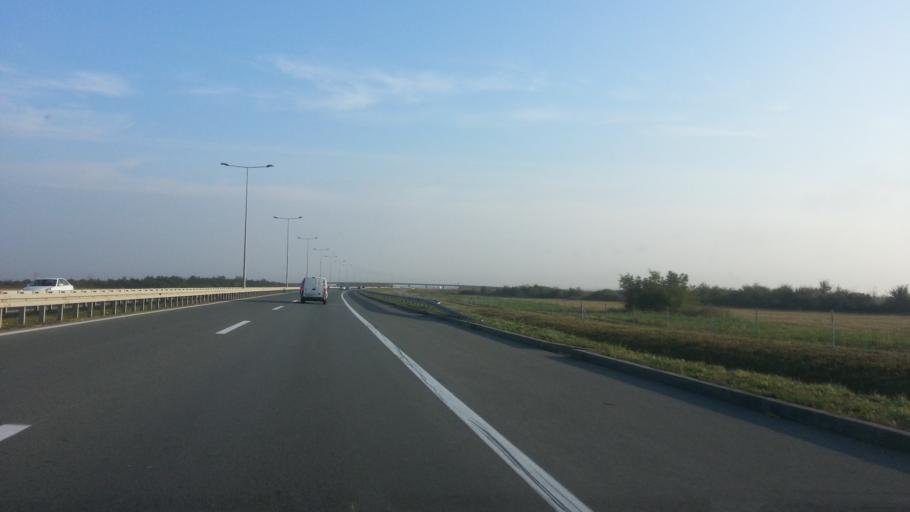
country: RS
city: Dobanovci
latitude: 44.8577
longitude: 20.2502
